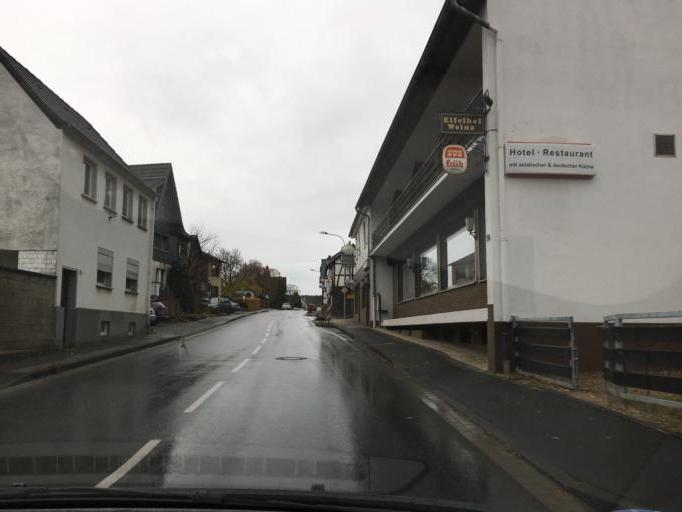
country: DE
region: North Rhine-Westphalia
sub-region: Regierungsbezirk Koln
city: Kall
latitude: 50.6210
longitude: 6.5438
